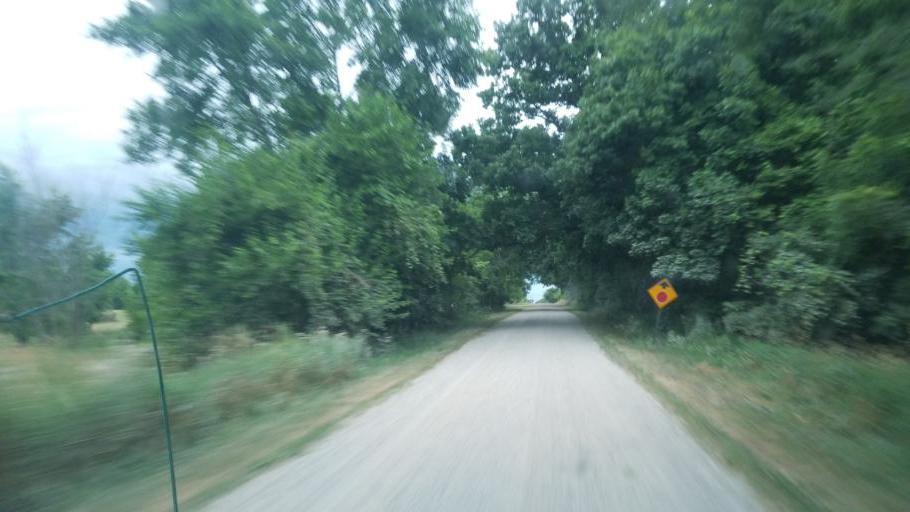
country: US
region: Ohio
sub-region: Defiance County
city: Hicksville
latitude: 41.3287
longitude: -84.8263
